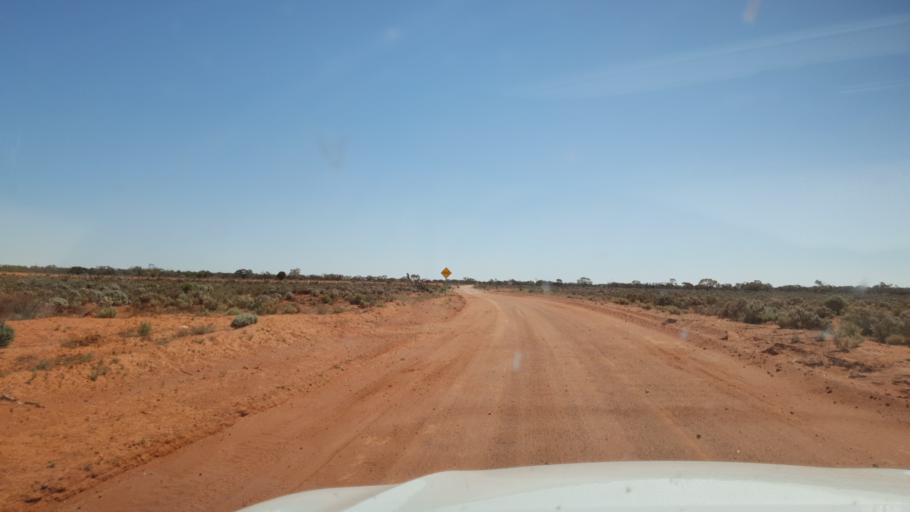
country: AU
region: South Australia
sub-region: Whyalla
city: Whyalla
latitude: -32.6542
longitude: 137.0354
